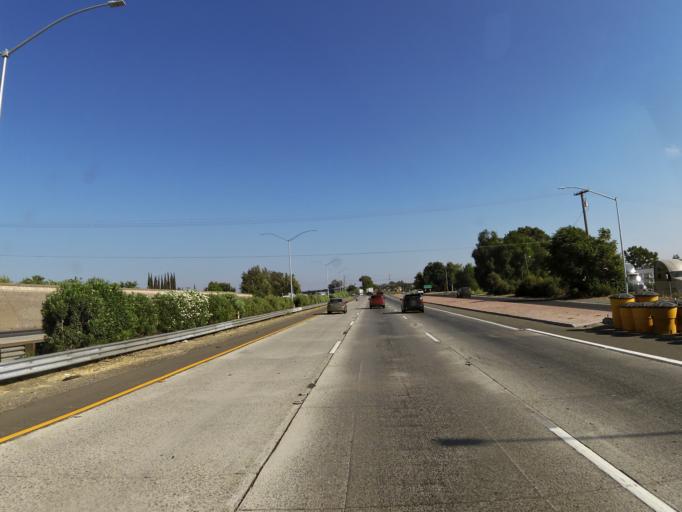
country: US
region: California
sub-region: Stanislaus County
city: Bystrom
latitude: 37.6136
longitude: -120.9803
